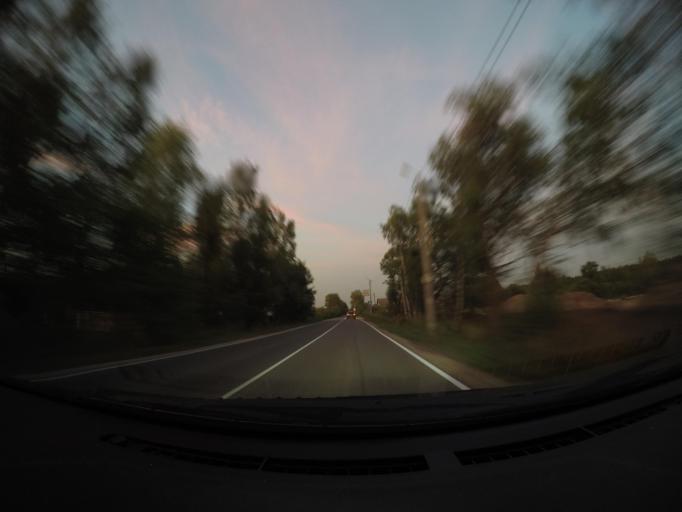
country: RU
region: Moskovskaya
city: Malyshevo
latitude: 55.5382
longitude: 38.4117
